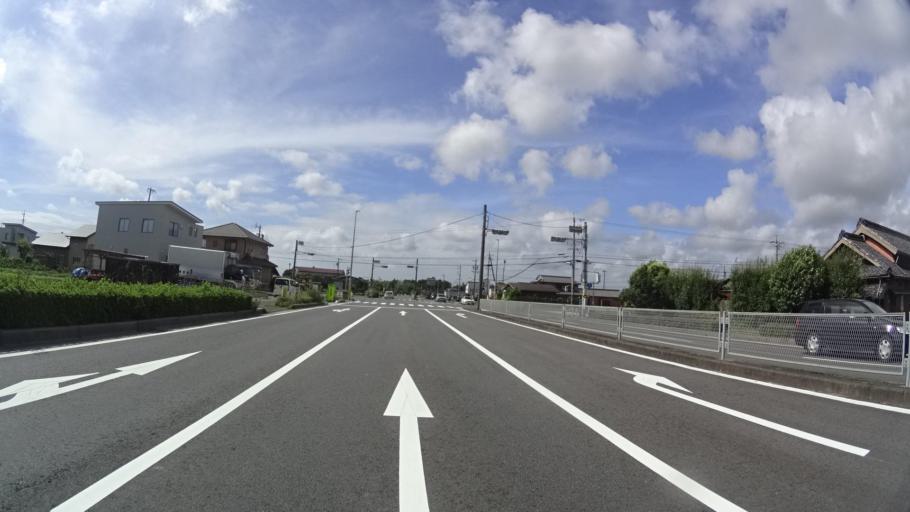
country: JP
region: Mie
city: Kameyama
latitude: 34.9020
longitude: 136.5033
